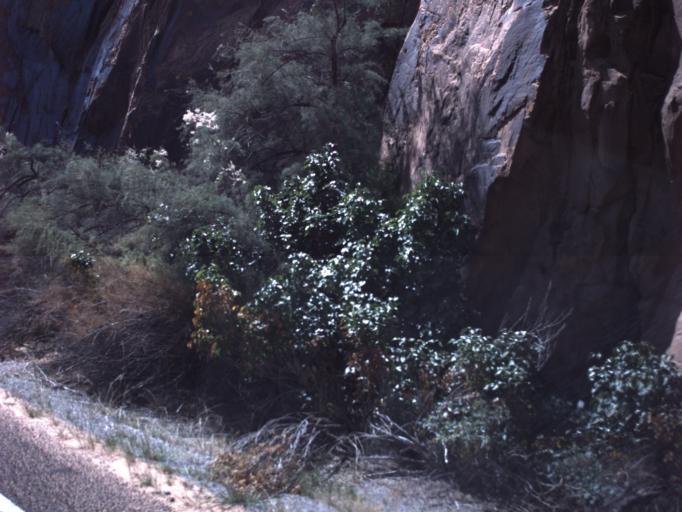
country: US
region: Utah
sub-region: Grand County
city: Moab
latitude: 38.5486
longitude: -109.5980
